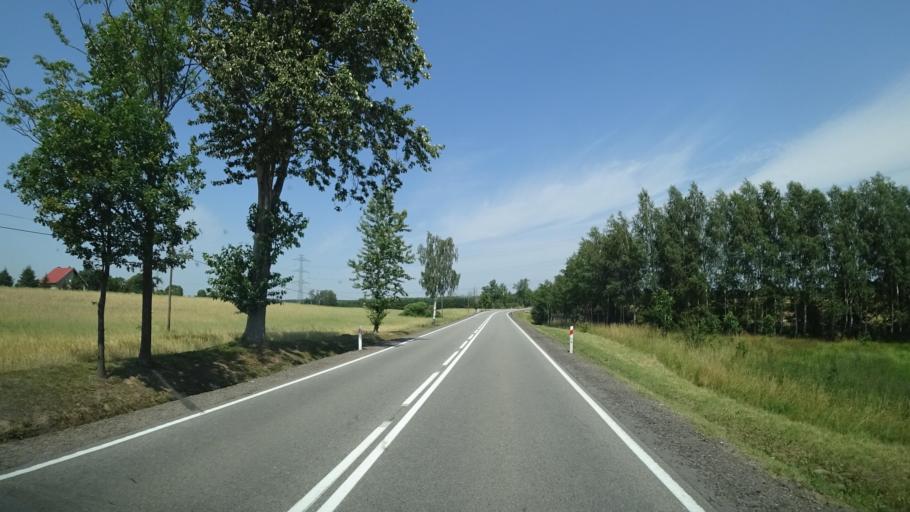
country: PL
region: Pomeranian Voivodeship
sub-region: Powiat koscierski
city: Koscierzyna
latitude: 54.1531
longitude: 18.0308
